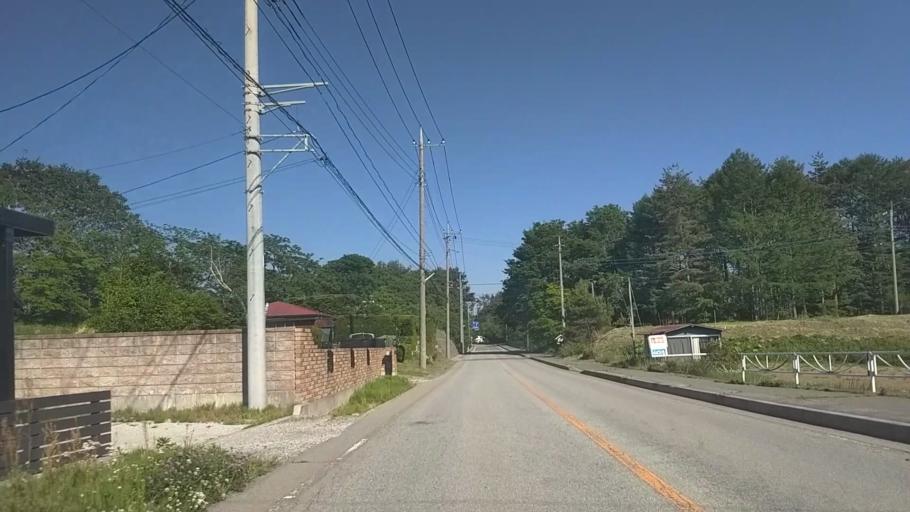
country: JP
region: Nagano
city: Chino
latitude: 35.8604
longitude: 138.3043
